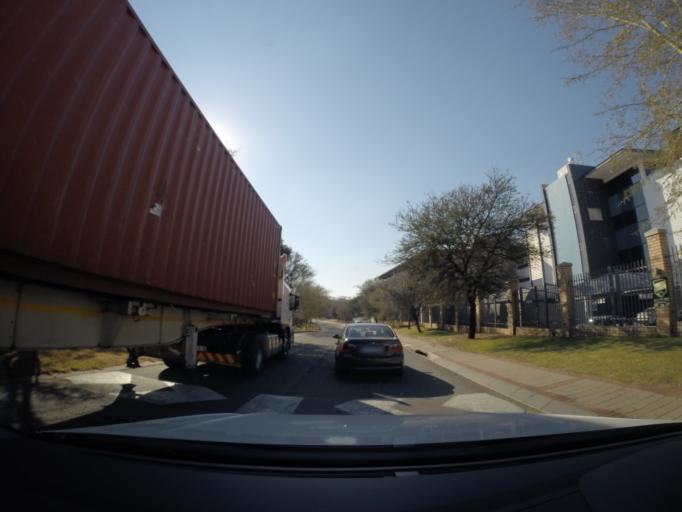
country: ZA
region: Gauteng
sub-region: City of Johannesburg Metropolitan Municipality
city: Modderfontein
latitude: -26.0952
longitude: 28.1249
